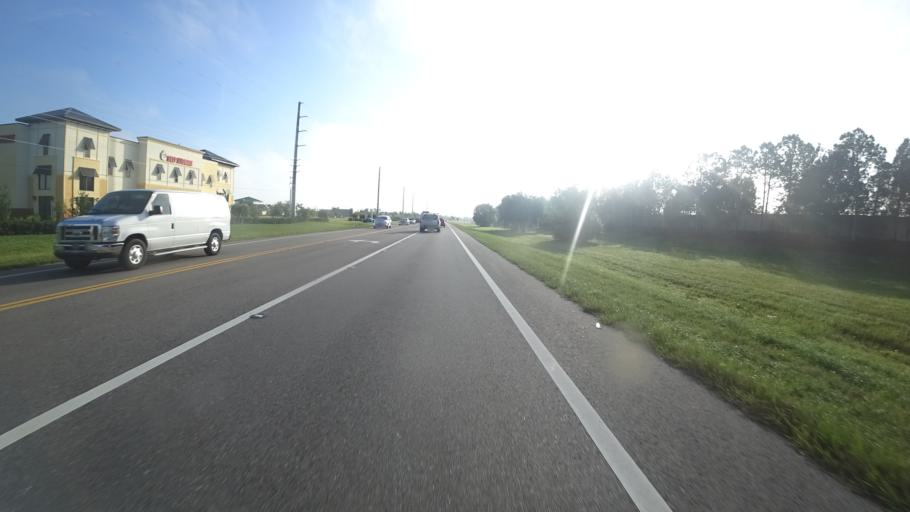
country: US
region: Florida
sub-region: Sarasota County
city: The Meadows
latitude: 27.4322
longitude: -82.3898
